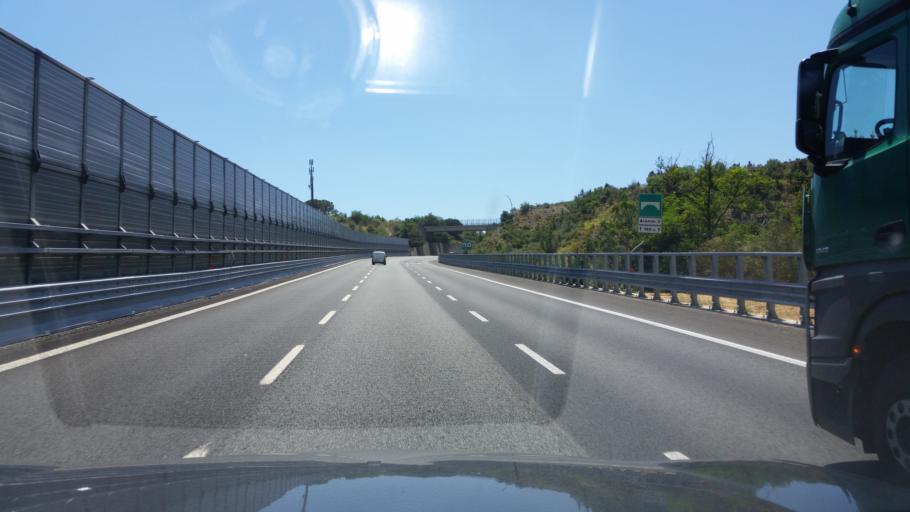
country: IT
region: Liguria
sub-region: Provincia di Genova
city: Sciarborasca
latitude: 44.3777
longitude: 8.6215
